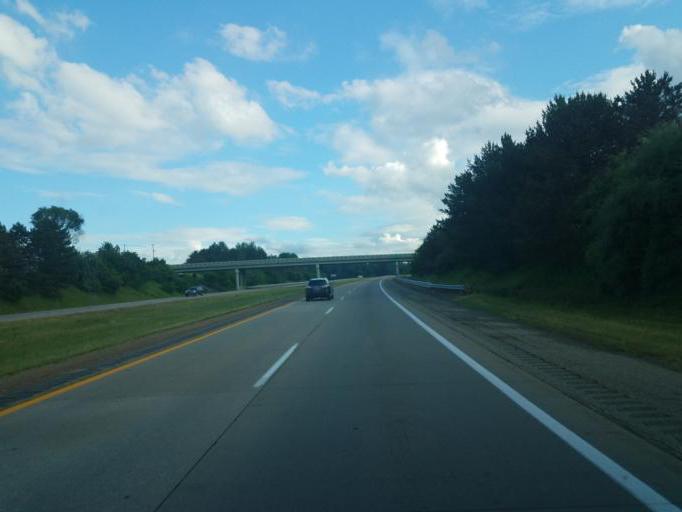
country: US
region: Indiana
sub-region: Steuben County
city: Fremont
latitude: 41.7668
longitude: -84.9876
